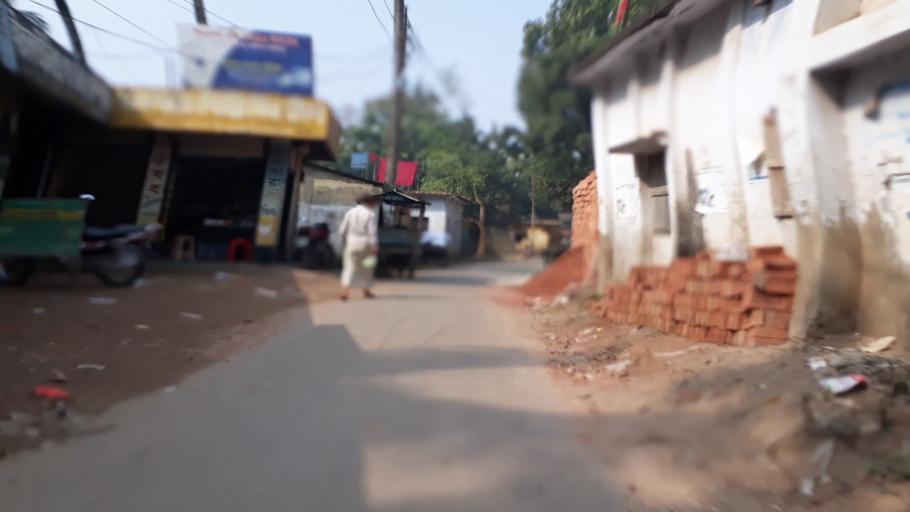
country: BD
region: Khulna
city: Kaliganj
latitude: 23.3550
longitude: 88.9147
